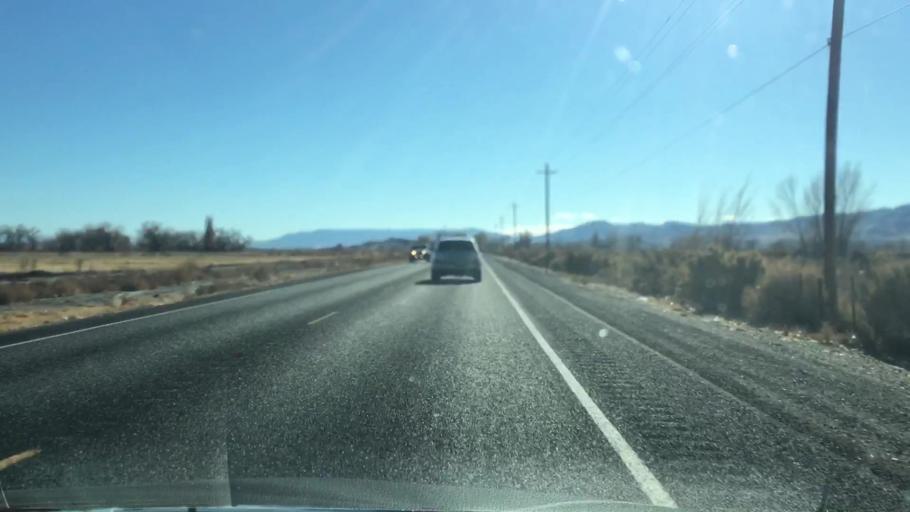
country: US
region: Nevada
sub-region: Lyon County
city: Yerington
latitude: 39.0584
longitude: -119.1814
